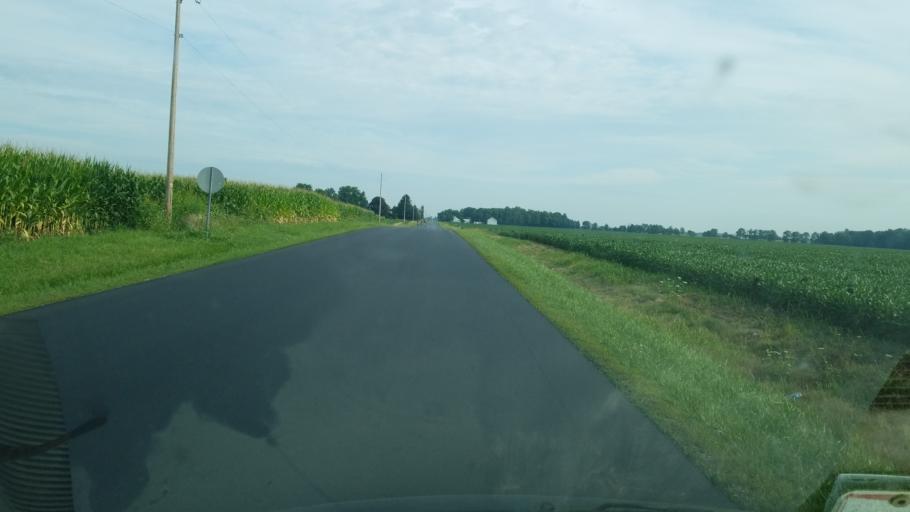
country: US
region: Ohio
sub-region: Crawford County
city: Bucyrus
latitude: 40.8493
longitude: -83.0165
